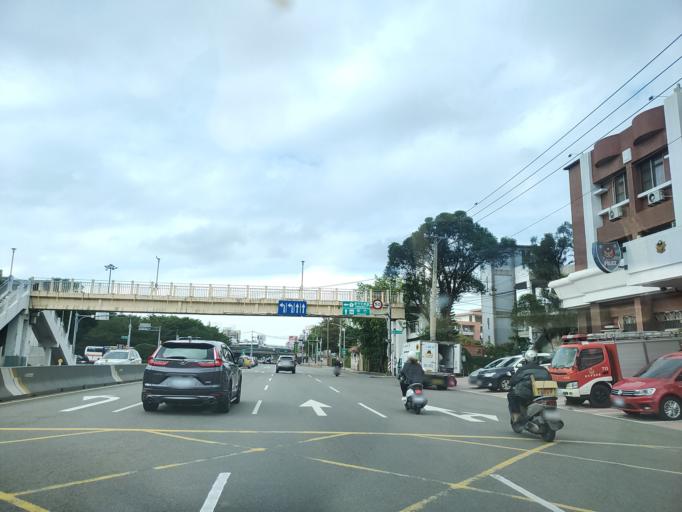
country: TW
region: Taiwan
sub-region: Hsinchu
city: Hsinchu
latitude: 24.7888
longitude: 121.0079
